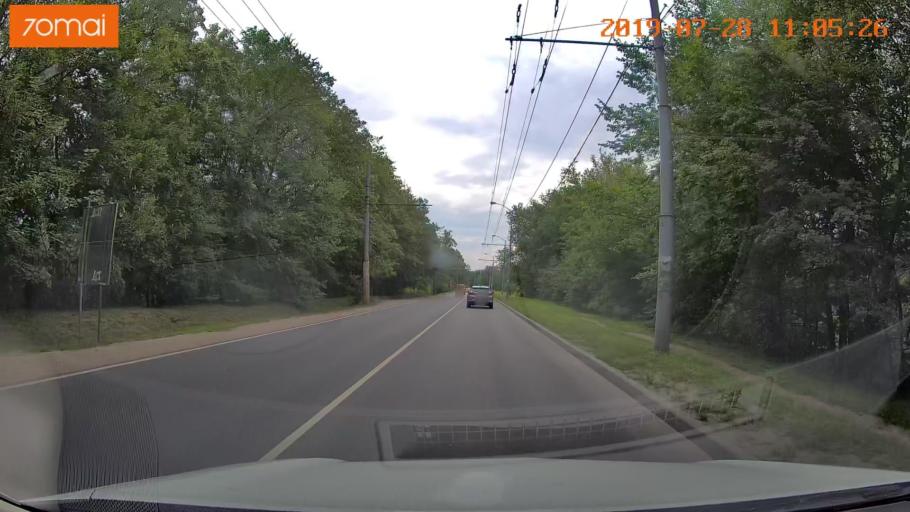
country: RU
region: Kaliningrad
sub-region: Gorod Kaliningrad
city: Kaliningrad
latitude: 54.7181
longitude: 20.3927
